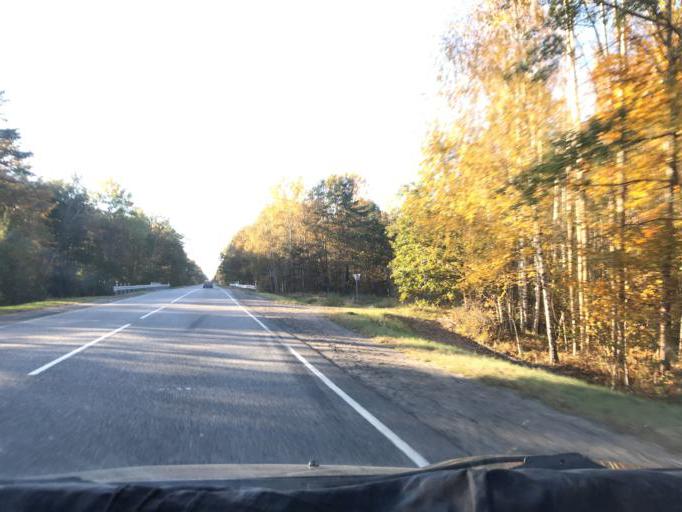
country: BY
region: Gomel
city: Pyetrykaw
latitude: 52.2600
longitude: 28.3308
